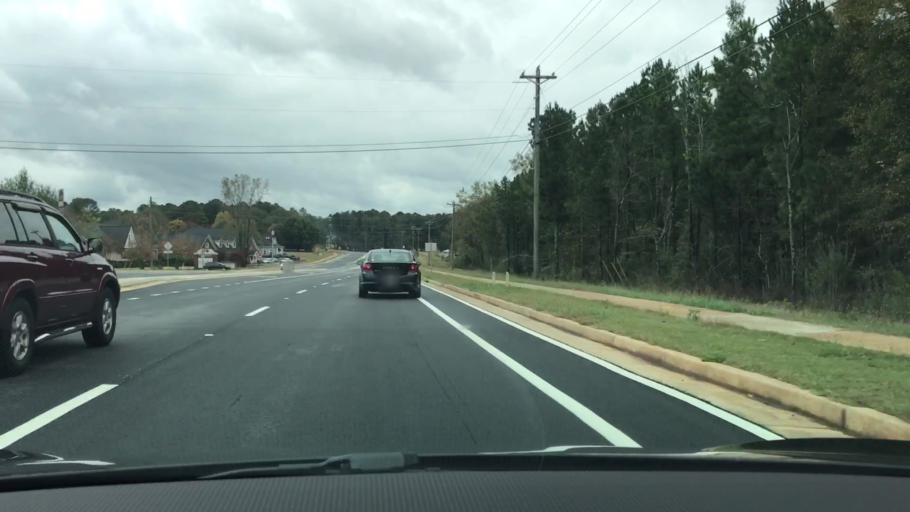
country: US
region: Georgia
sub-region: Oconee County
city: Watkinsville
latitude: 33.8863
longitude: -83.4559
